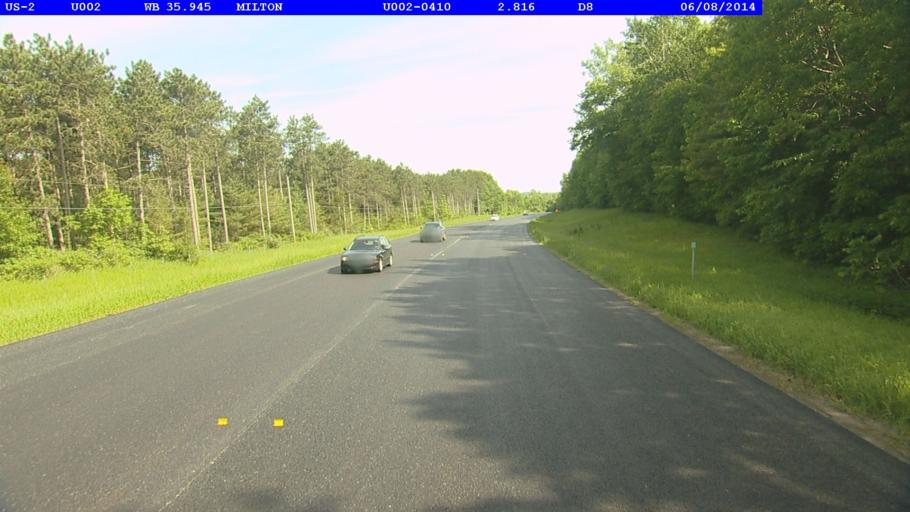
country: US
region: Vermont
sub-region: Chittenden County
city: Colchester
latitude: 44.6148
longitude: -73.2121
